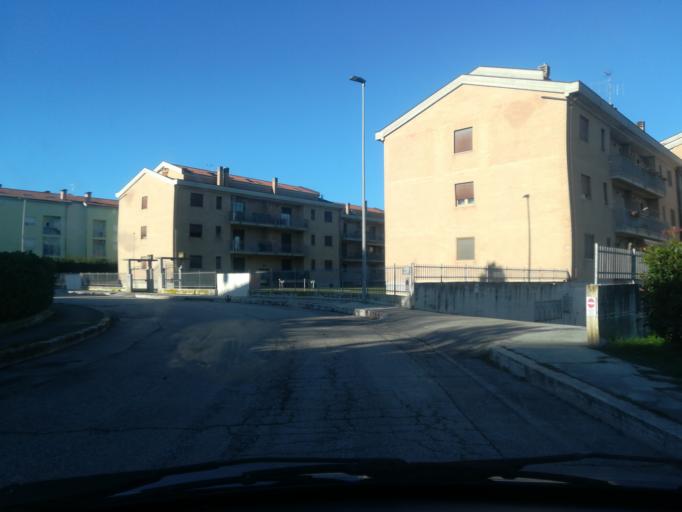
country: IT
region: The Marches
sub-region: Provincia di Macerata
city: Piediripa
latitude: 43.2763
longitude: 13.4790
